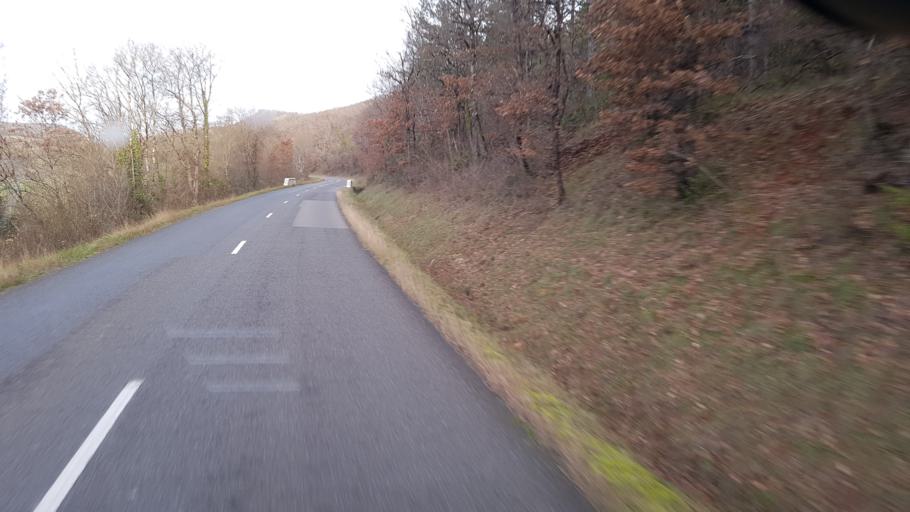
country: FR
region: Midi-Pyrenees
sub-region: Departement du Tarn-et-Garonne
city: Monclar-de-Quercy
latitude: 43.9764
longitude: 1.7265
